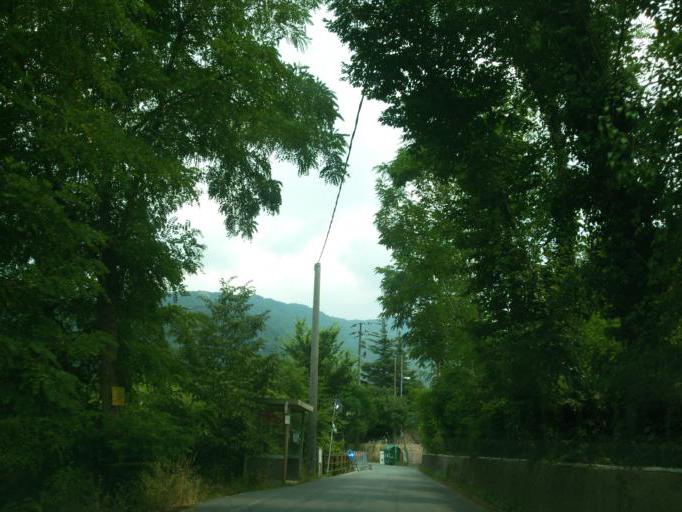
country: IT
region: Liguria
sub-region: Provincia di Genova
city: Piccarello
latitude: 44.4337
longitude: 9.0159
